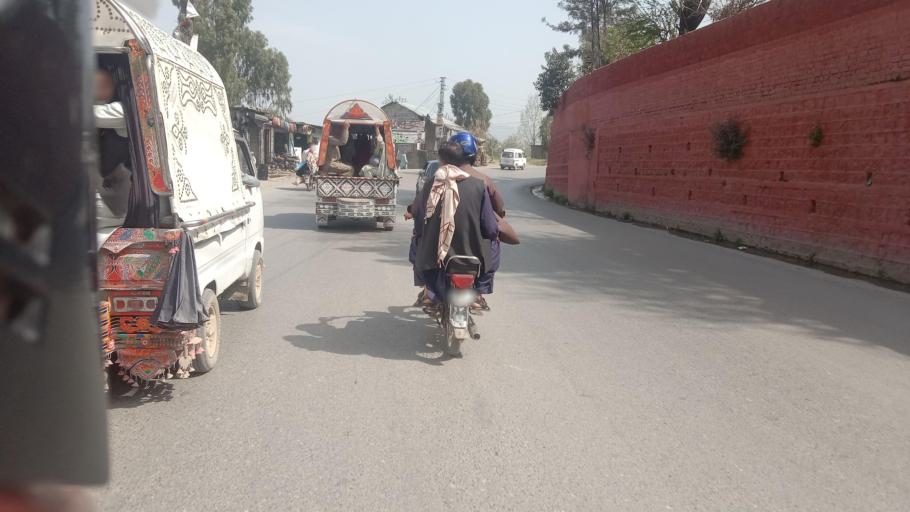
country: PK
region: Khyber Pakhtunkhwa
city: Abbottabad
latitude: 34.1264
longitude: 73.1939
